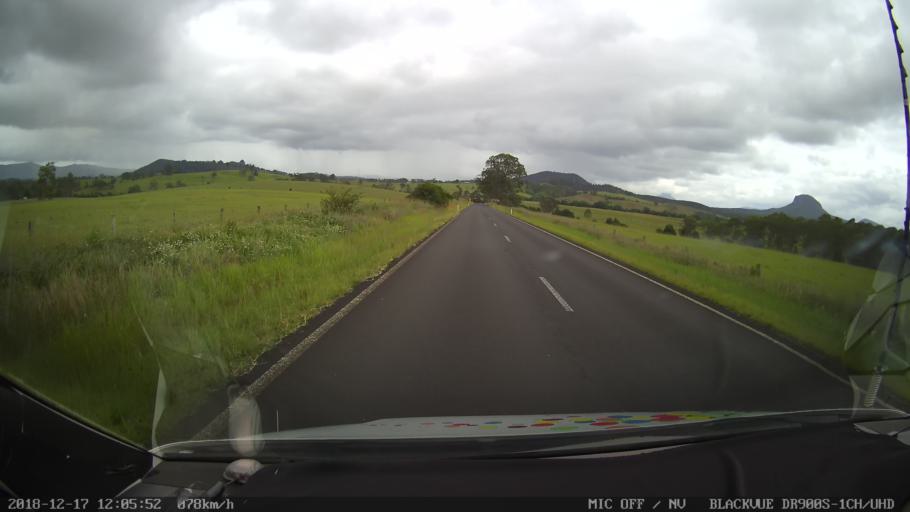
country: AU
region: New South Wales
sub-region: Kyogle
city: Kyogle
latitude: -28.4883
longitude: 152.5672
